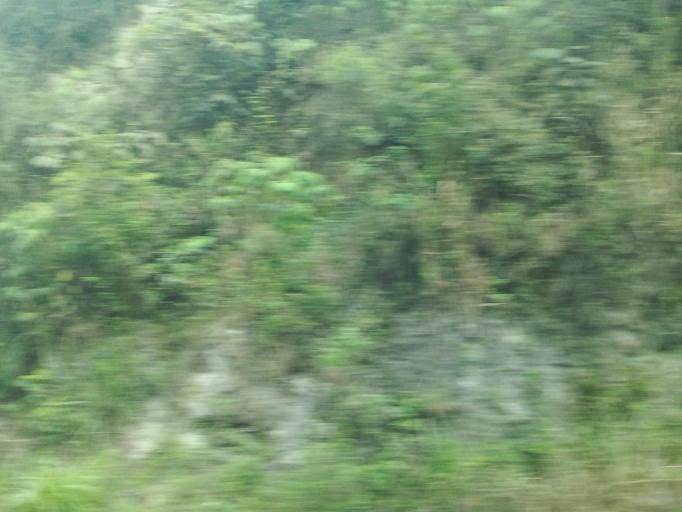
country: BR
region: Minas Gerais
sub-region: Joao Monlevade
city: Joao Monlevade
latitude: -19.8257
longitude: -43.1254
